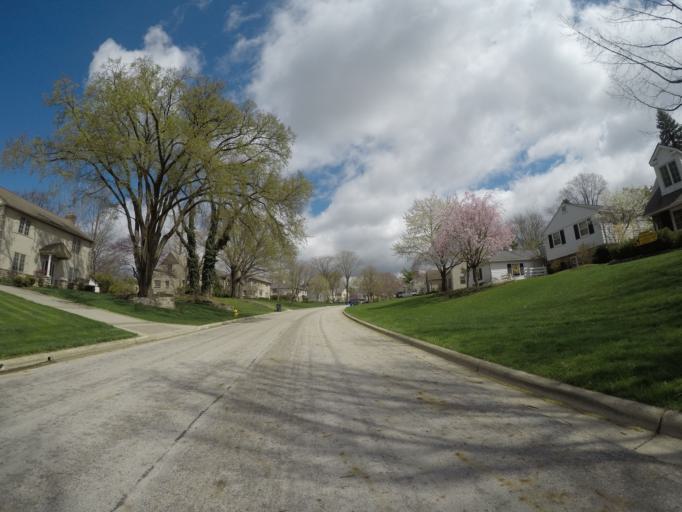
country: US
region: Ohio
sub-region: Franklin County
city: Upper Arlington
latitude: 39.9962
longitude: -83.0679
